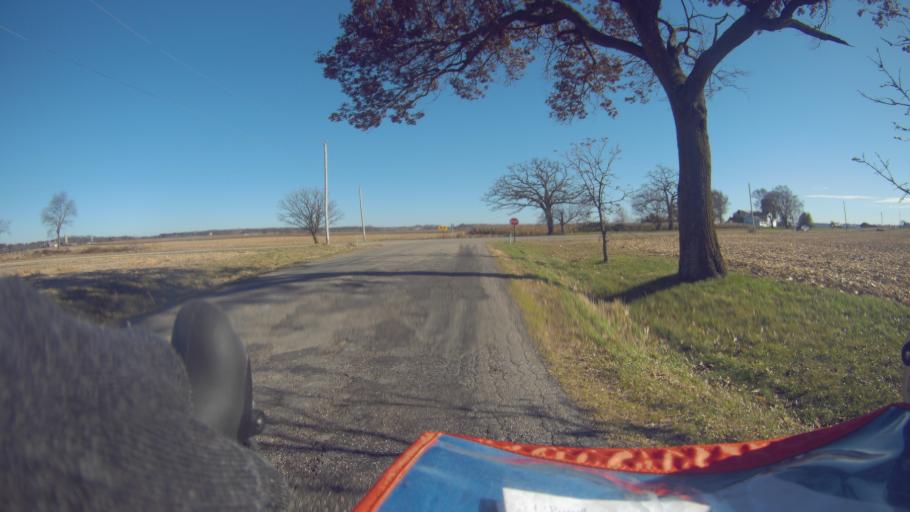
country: US
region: Wisconsin
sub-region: Green County
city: Brooklyn
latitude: 42.8708
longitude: -89.3945
